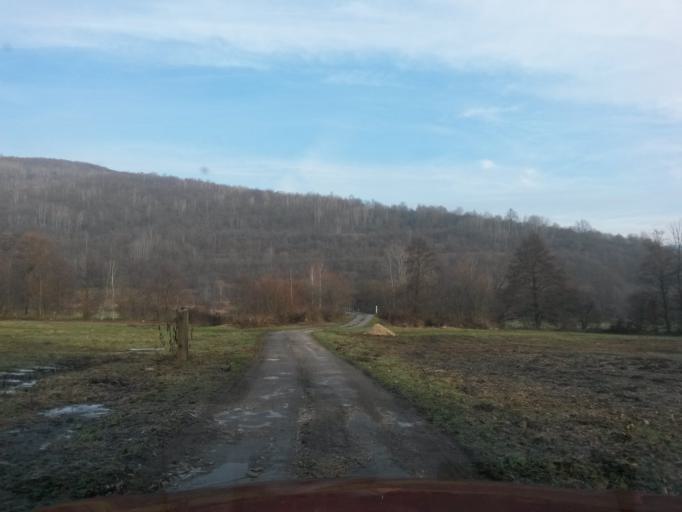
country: SK
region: Kosicky
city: Roznava
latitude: 48.7107
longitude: 20.4627
